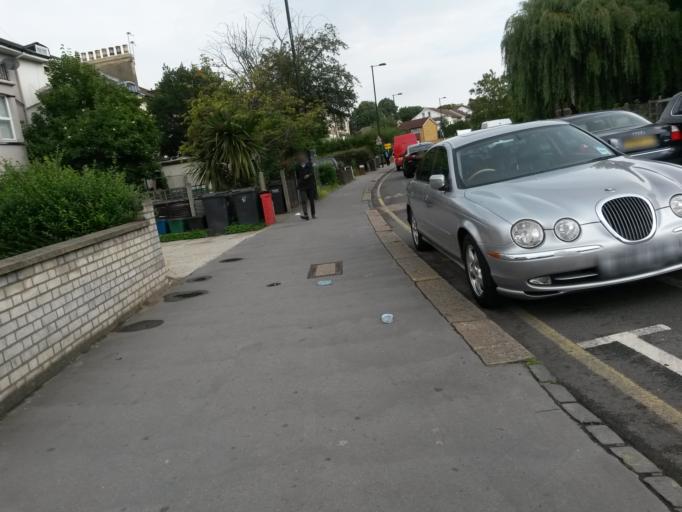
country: GB
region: England
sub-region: Greater London
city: Thornton Heath
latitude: 51.3927
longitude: -0.0876
